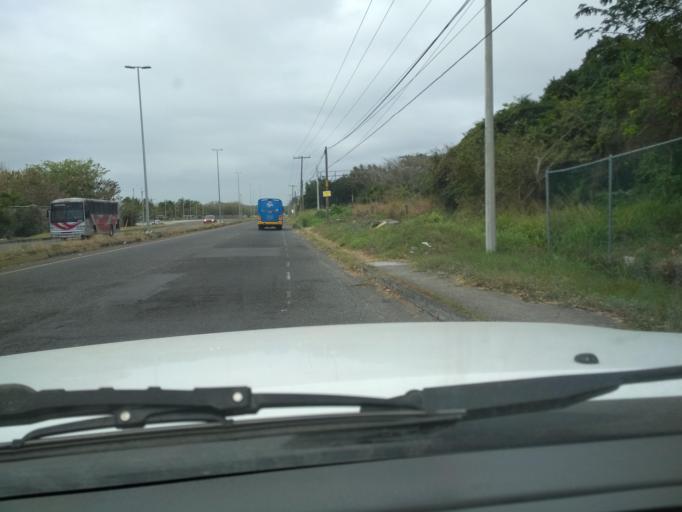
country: MX
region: Veracruz
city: Boca del Rio
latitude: 19.0946
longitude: -96.1097
